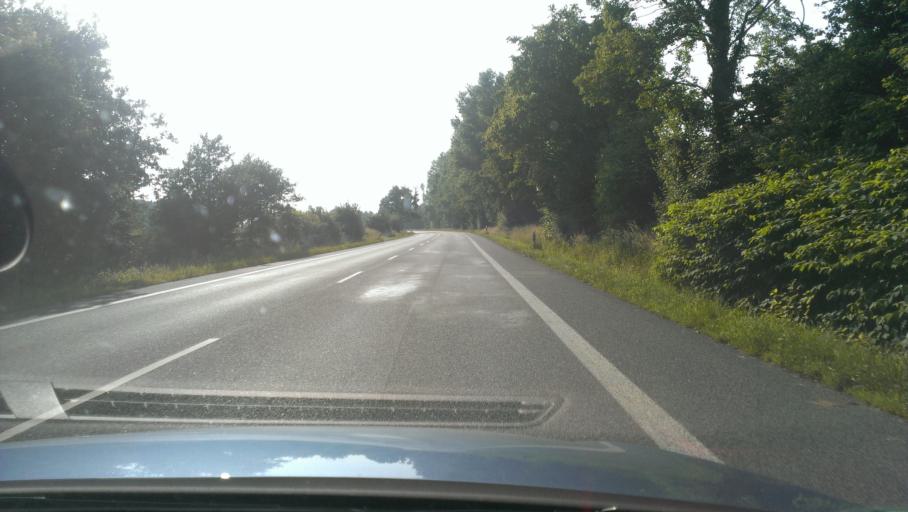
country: DE
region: North Rhine-Westphalia
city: Ahlen
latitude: 51.8247
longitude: 7.8965
